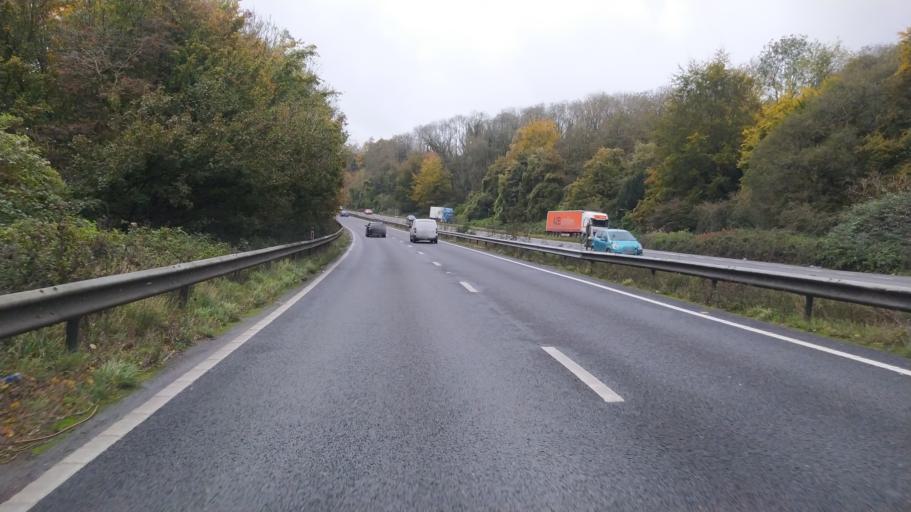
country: GB
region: England
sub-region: Hampshire
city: Petersfield
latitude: 50.9554
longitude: -0.9812
